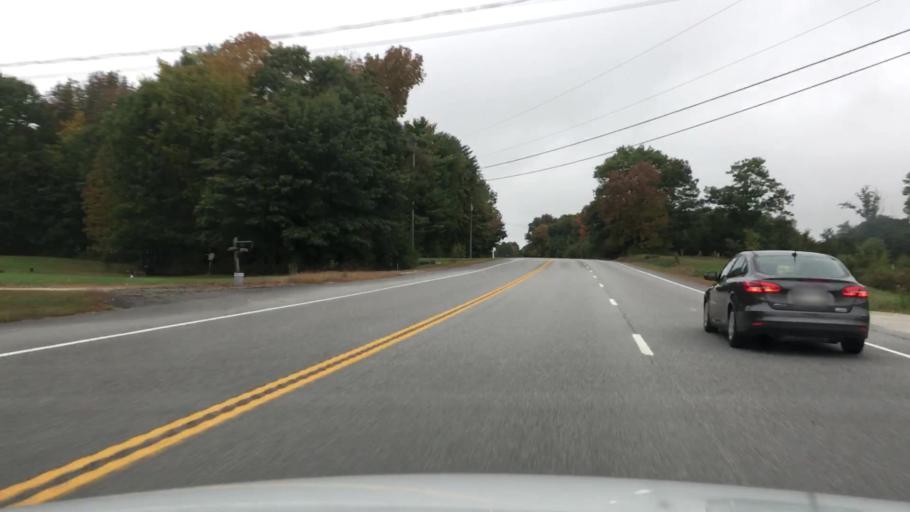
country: US
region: Maine
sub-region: Androscoggin County
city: Poland
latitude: 44.0847
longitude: -70.4194
